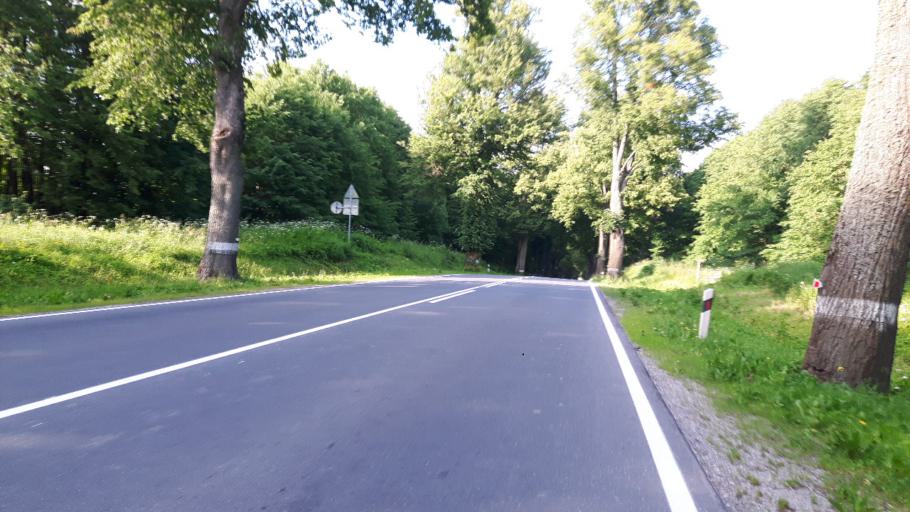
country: RU
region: Kaliningrad
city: Ladushkin
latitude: 54.5263
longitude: 20.1202
